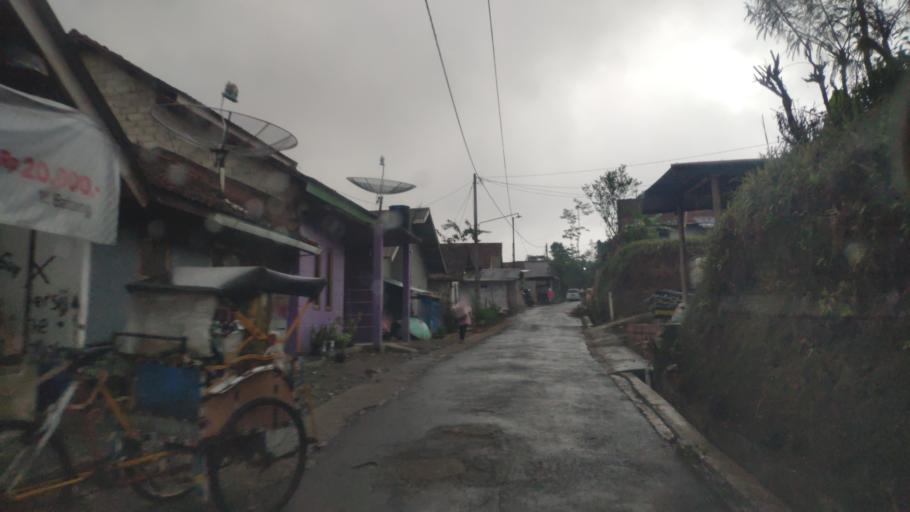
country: ID
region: Central Java
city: Wonosobo
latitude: -7.2741
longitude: 109.7386
